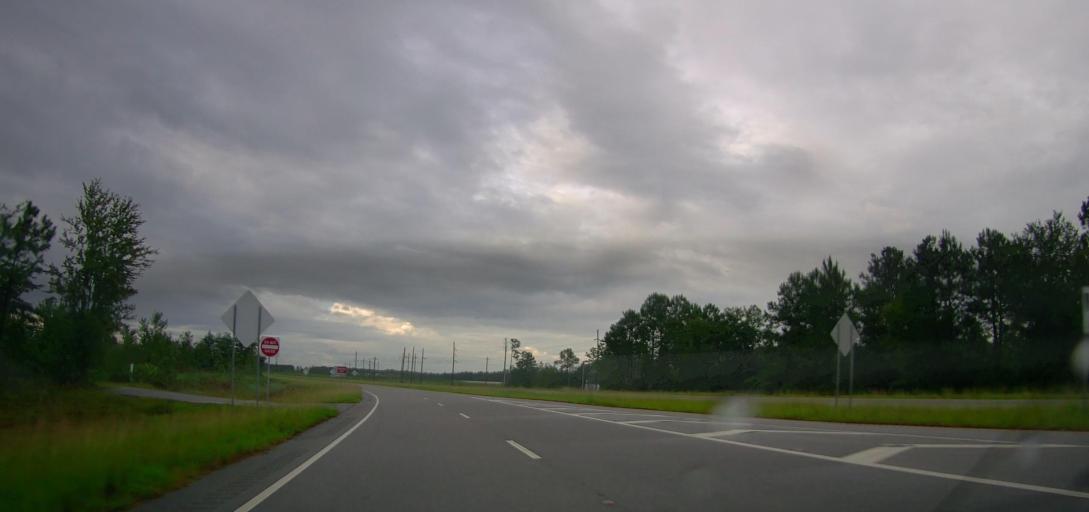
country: US
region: Georgia
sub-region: Ware County
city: Deenwood
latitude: 31.2458
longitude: -82.4291
